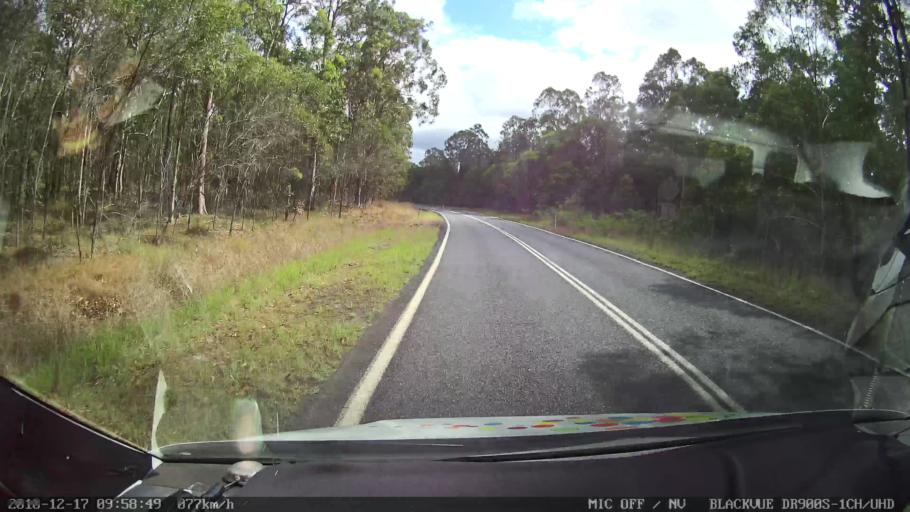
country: AU
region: New South Wales
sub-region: Tenterfield Municipality
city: Carrolls Creek
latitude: -28.9176
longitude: 152.4134
